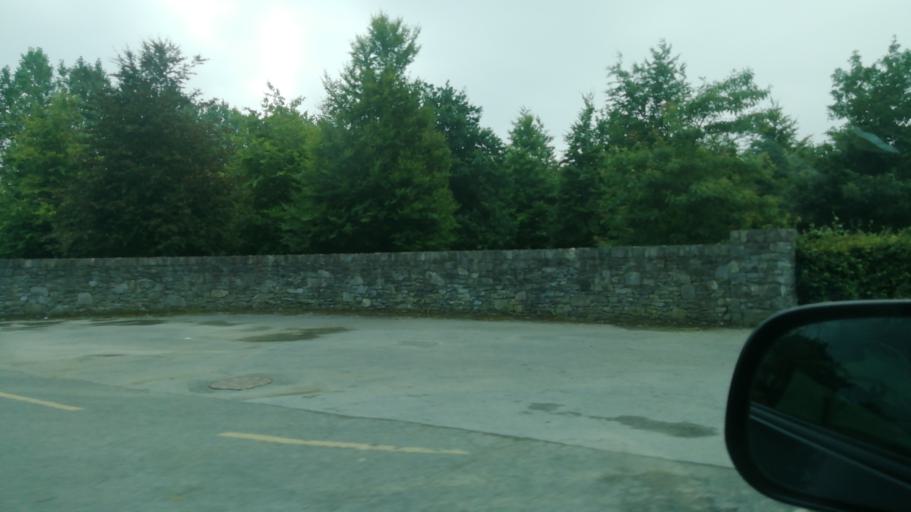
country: IE
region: Munster
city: Fethard
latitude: 52.4926
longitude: -7.6902
